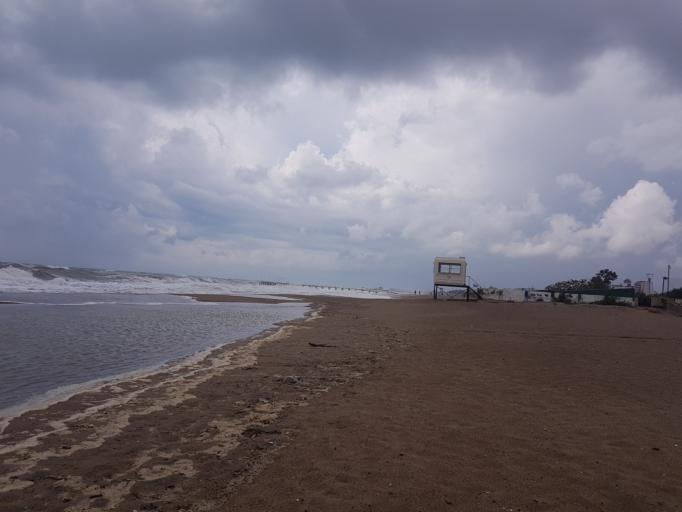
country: TR
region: Antalya
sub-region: Serik
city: Kumkoey
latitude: 36.8537
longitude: 30.9047
